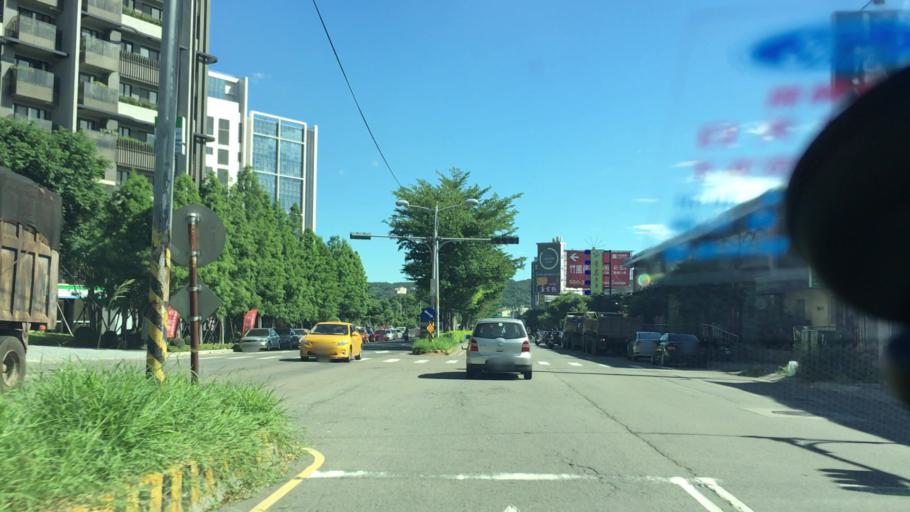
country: TW
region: Taiwan
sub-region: Hsinchu
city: Zhubei
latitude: 24.8381
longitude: 121.0211
